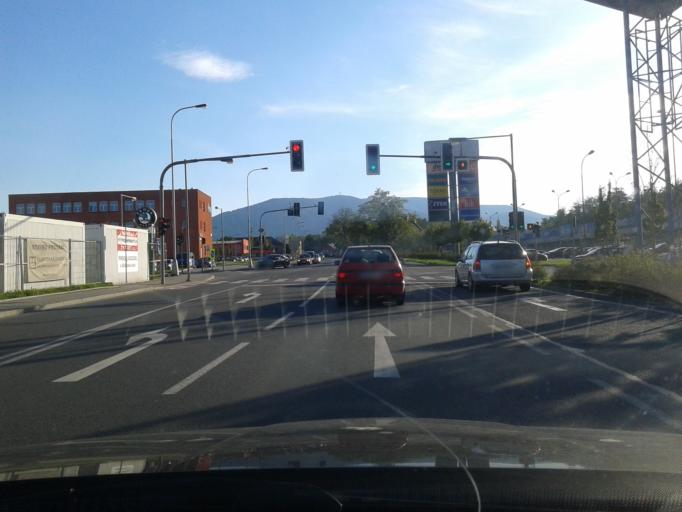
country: CZ
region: Moravskoslezsky
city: Trinec
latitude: 49.6750
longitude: 18.6620
